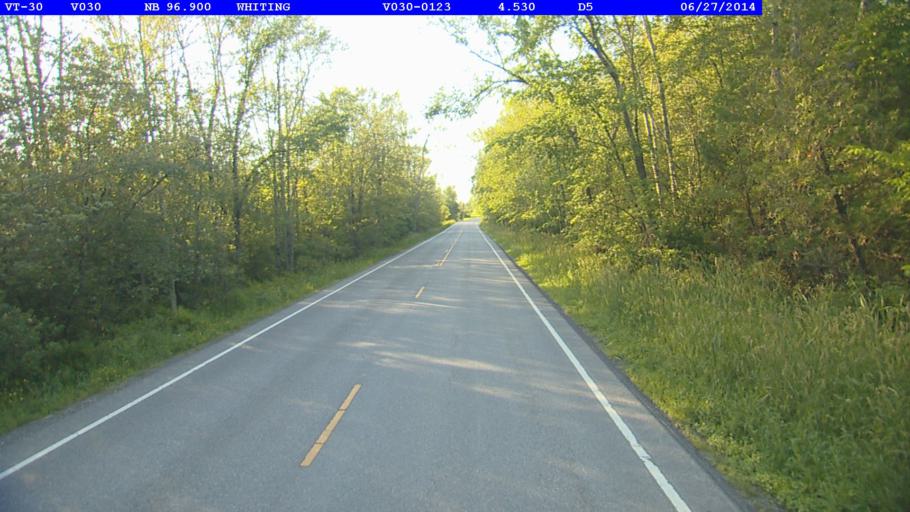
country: US
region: Vermont
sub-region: Addison County
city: Middlebury (village)
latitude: 43.9022
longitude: -73.2066
